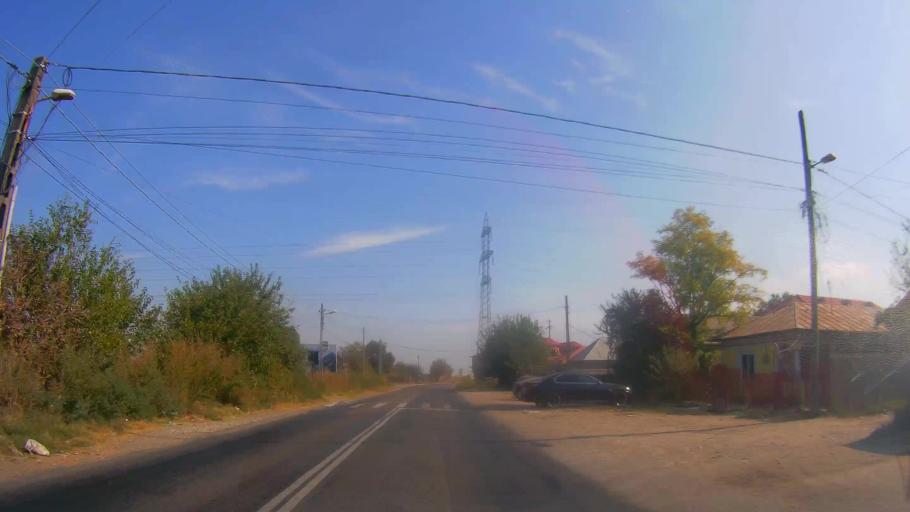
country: RO
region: Giurgiu
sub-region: Comuna Fratesti
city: Remus
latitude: 43.9126
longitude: 25.9846
